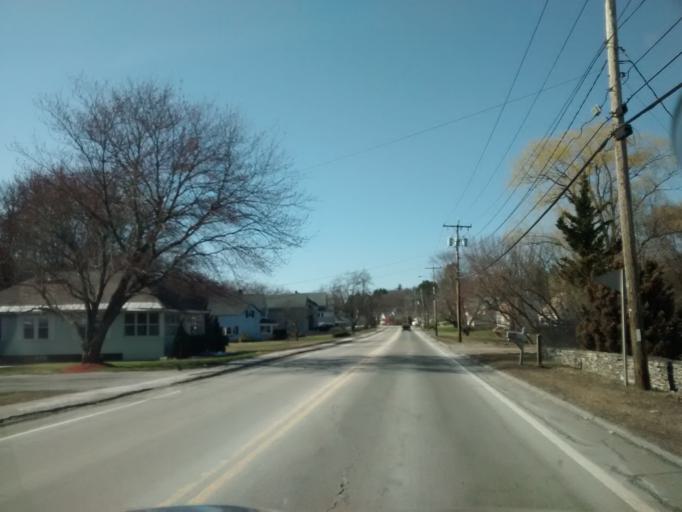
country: US
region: Massachusetts
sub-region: Worcester County
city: Millbury
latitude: 42.1993
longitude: -71.7711
